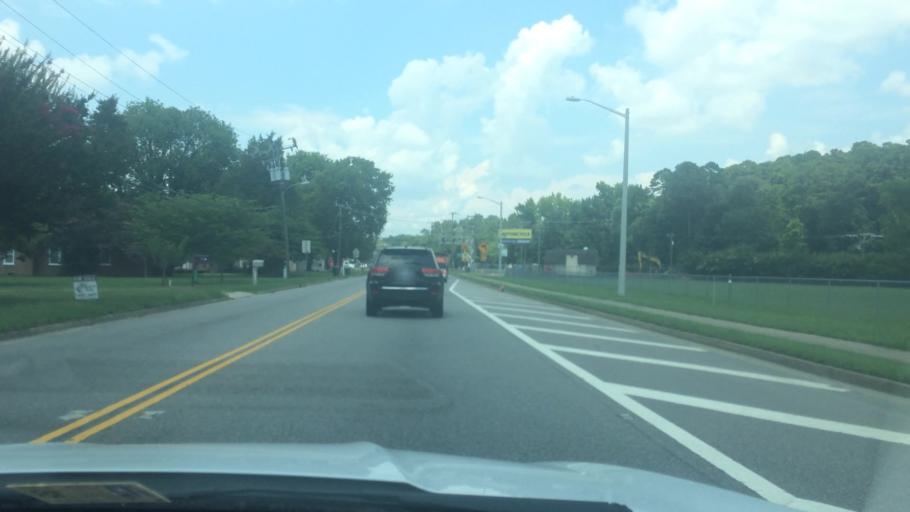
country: US
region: Virginia
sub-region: York County
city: Yorktown
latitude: 37.1897
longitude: -76.5717
